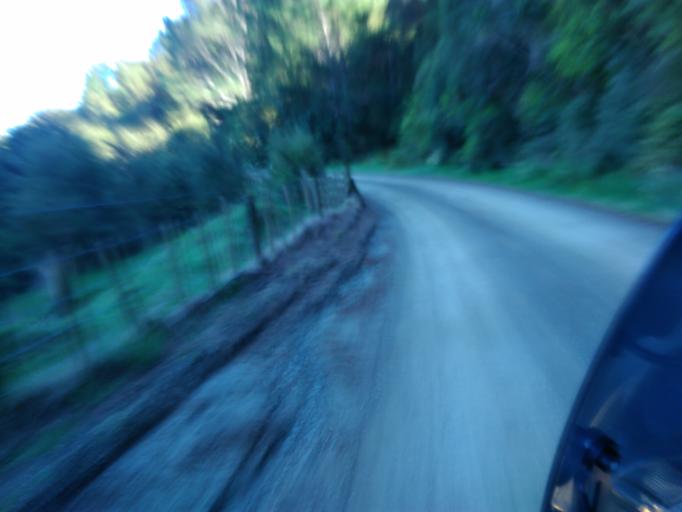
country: NZ
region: Gisborne
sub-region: Gisborne District
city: Gisborne
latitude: -38.4068
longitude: 177.6808
